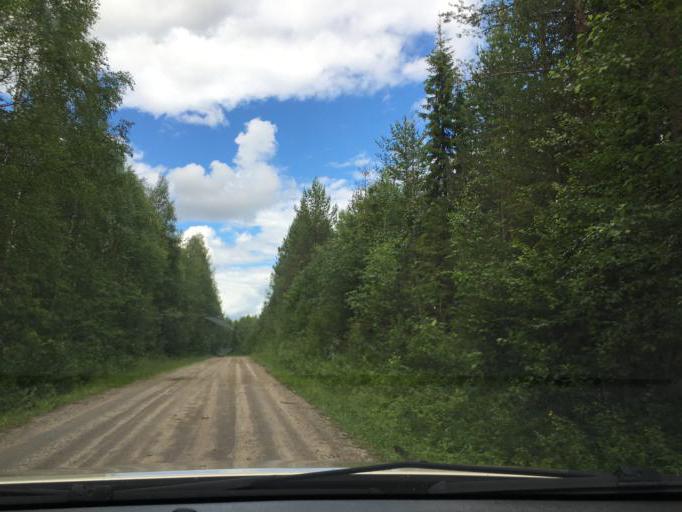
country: SE
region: Norrbotten
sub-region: Overkalix Kommun
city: OEverkalix
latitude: 66.1250
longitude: 22.7849
